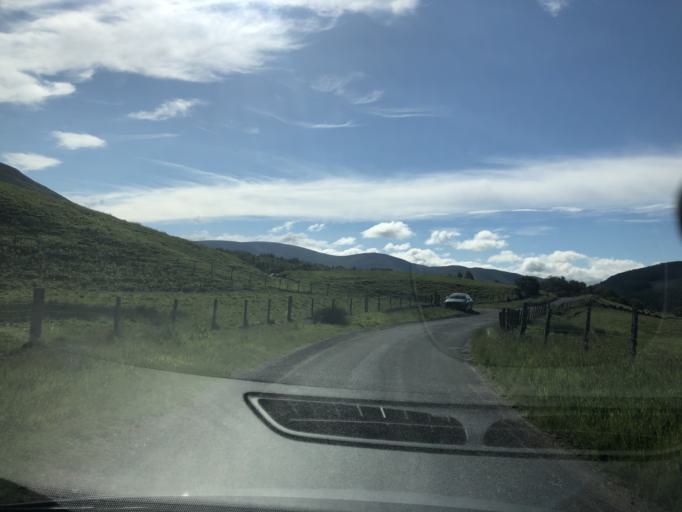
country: GB
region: Scotland
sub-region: Angus
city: Kirriemuir
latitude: 56.8419
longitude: -3.0950
